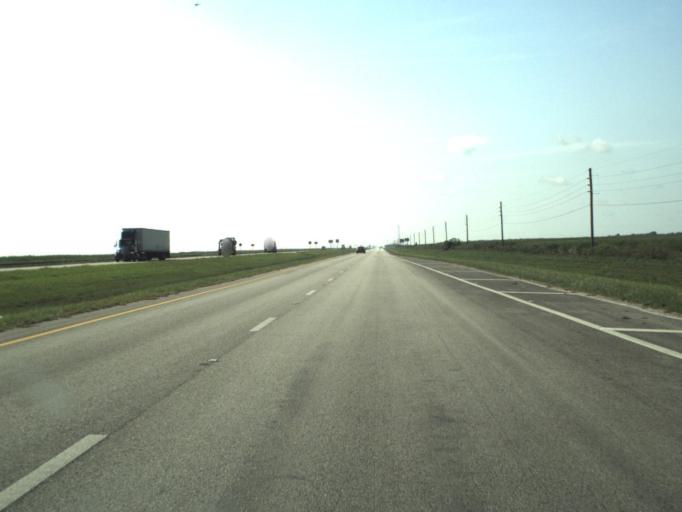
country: US
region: Florida
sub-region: Palm Beach County
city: Belle Glade Camp
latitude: 26.5337
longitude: -80.6921
